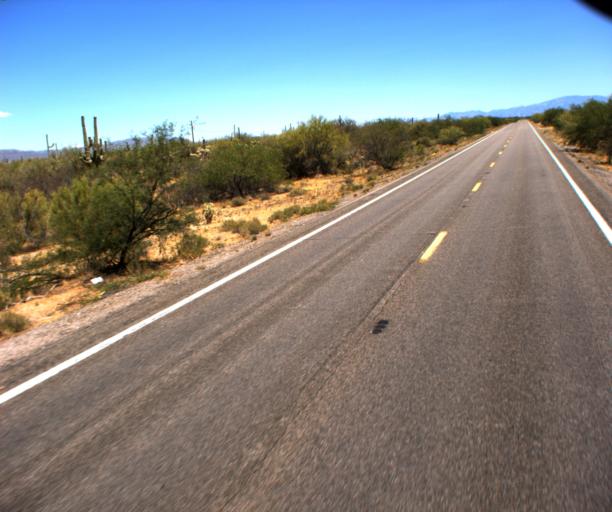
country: US
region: Arizona
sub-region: Pima County
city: Marana
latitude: 32.7584
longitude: -111.1435
